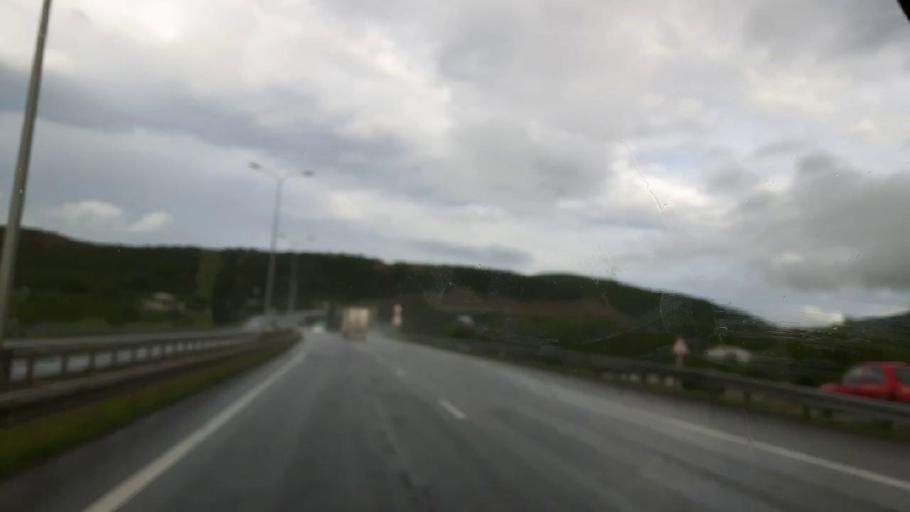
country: GE
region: Shida Kartli
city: Kaspi
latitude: 41.9945
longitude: 44.4151
